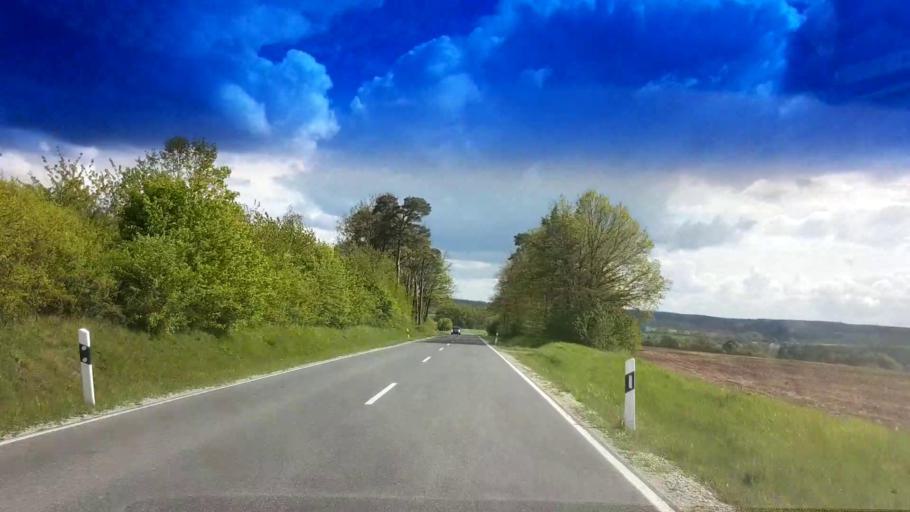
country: DE
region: Bavaria
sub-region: Upper Franconia
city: Stegaurach
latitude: 49.8347
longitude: 10.8392
